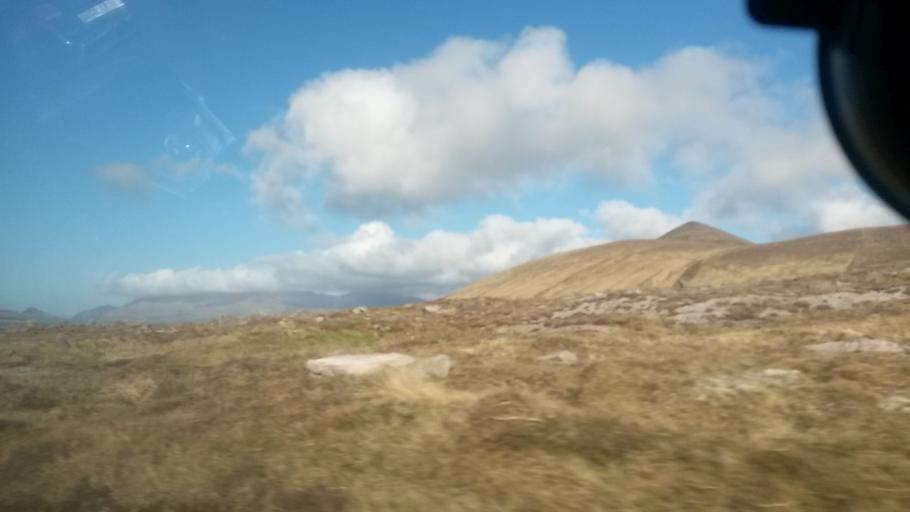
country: IE
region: Munster
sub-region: Ciarrai
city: Dingle
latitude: 52.1495
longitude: -10.4665
